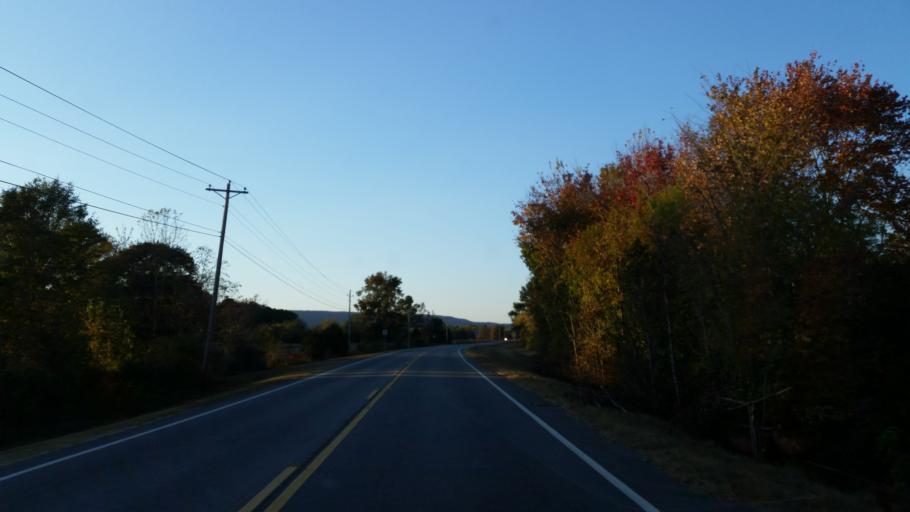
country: US
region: Georgia
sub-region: Gordon County
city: Calhoun
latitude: 34.5635
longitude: -85.0199
